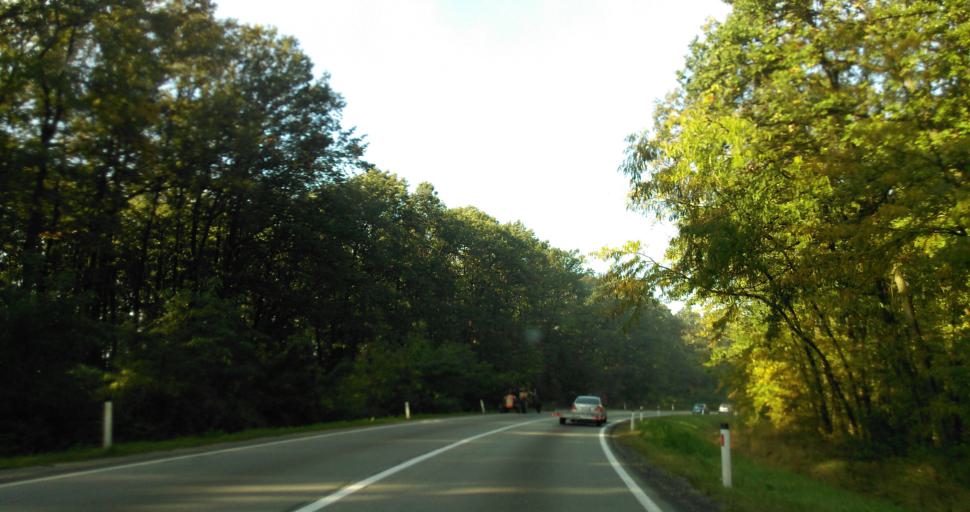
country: RS
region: Central Serbia
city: Sremcica
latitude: 44.6328
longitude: 20.3975
